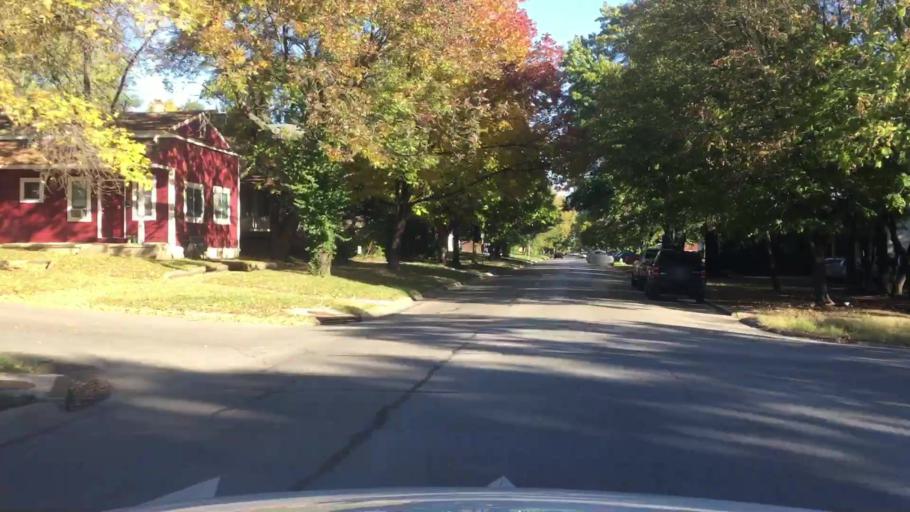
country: US
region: Kansas
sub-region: Douglas County
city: Lawrence
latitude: 38.9553
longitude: -95.2383
